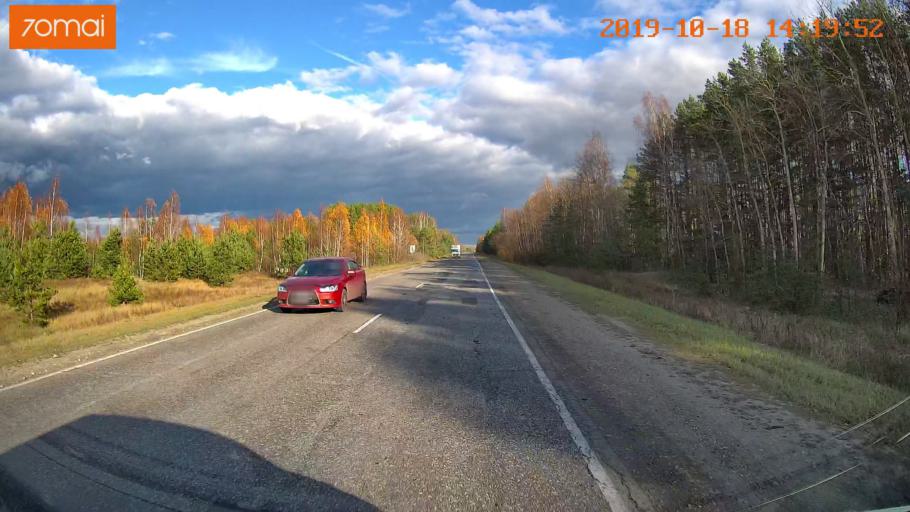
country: RU
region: Rjazan
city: Tuma
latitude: 55.1422
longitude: 40.4189
